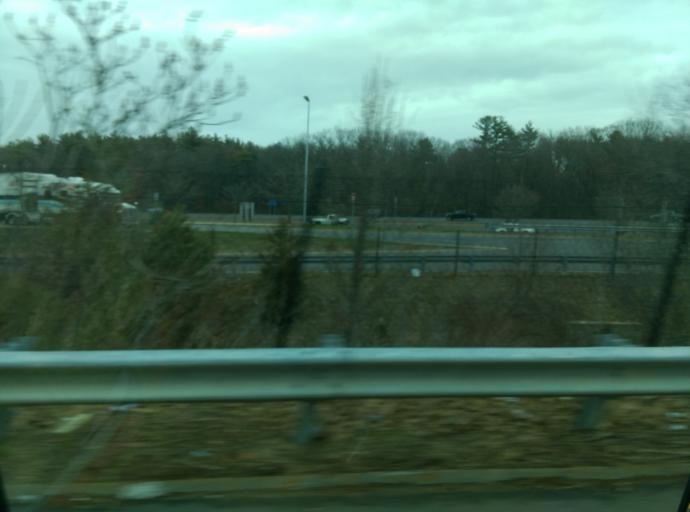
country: US
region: New Hampshire
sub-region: Rockingham County
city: Seabrook
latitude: 42.8787
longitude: -70.8851
